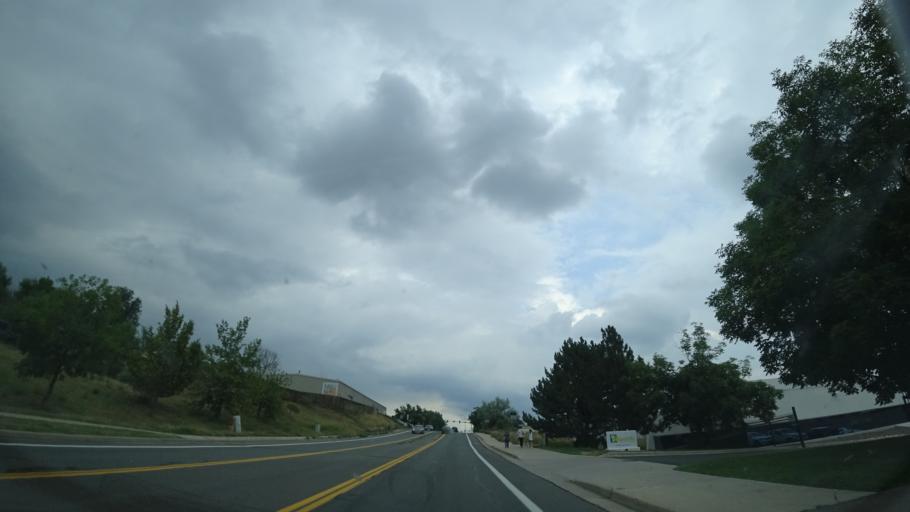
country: US
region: Colorado
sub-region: Jefferson County
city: West Pleasant View
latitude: 39.7105
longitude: -105.1381
